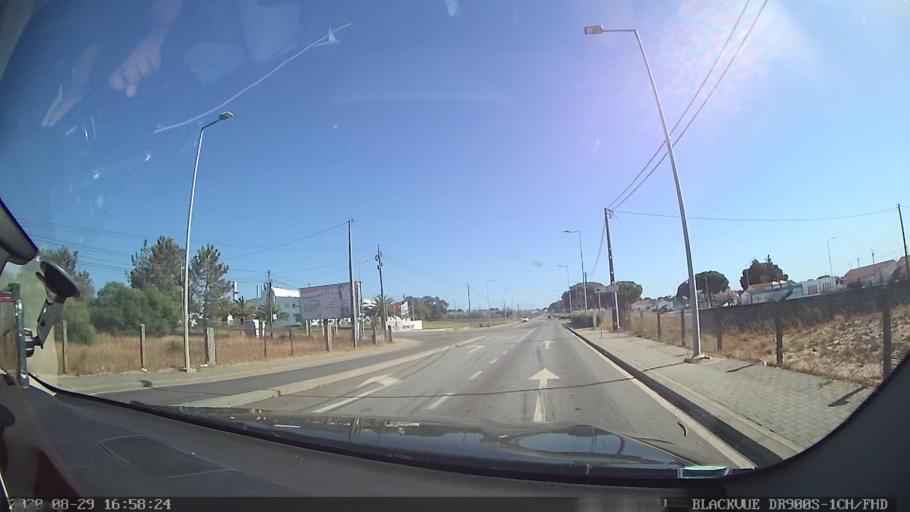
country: PT
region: Setubal
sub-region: Alcacer do Sal
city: Alcacer do Sal
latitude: 38.3963
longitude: -8.5143
